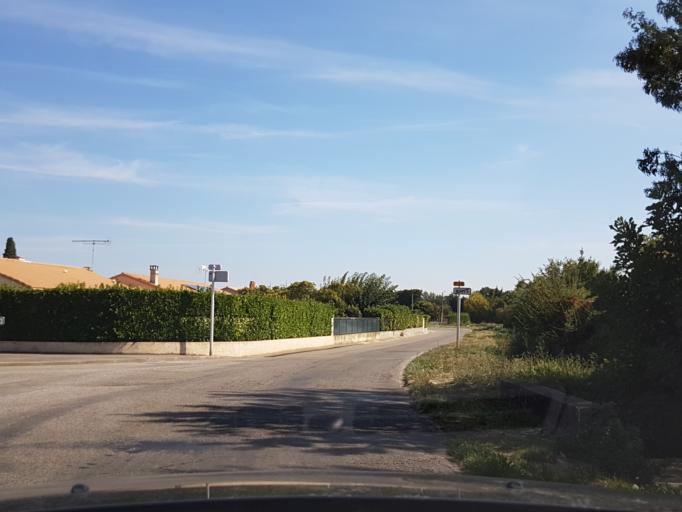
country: FR
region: Provence-Alpes-Cote d'Azur
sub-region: Departement des Bouches-du-Rhone
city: Noves
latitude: 43.8749
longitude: 4.9068
